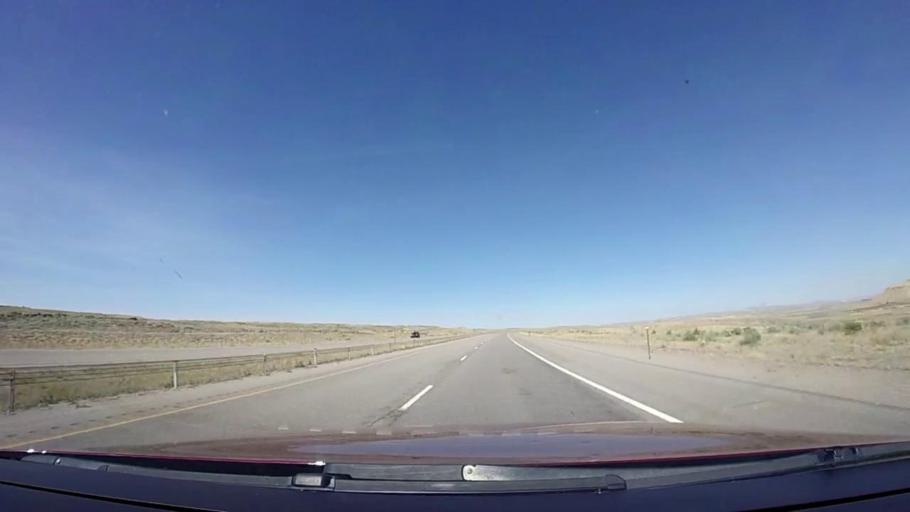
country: US
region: Wyoming
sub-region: Sweetwater County
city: Rock Springs
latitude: 41.6483
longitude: -108.6917
